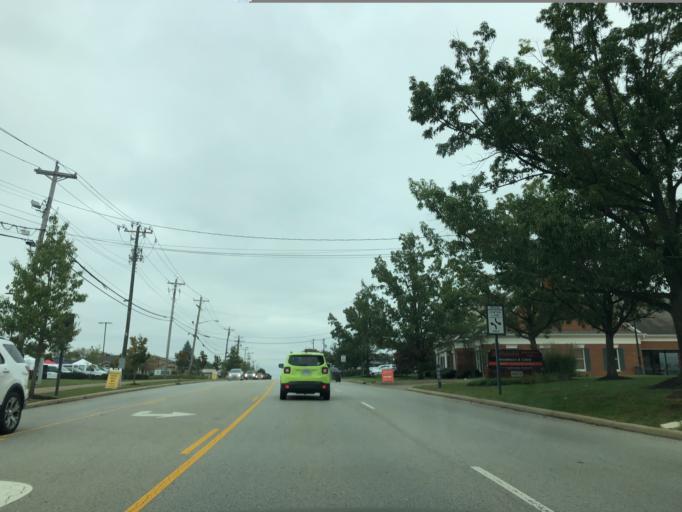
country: US
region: Ohio
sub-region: Hamilton County
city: Montgomery
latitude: 39.2299
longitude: -84.3533
